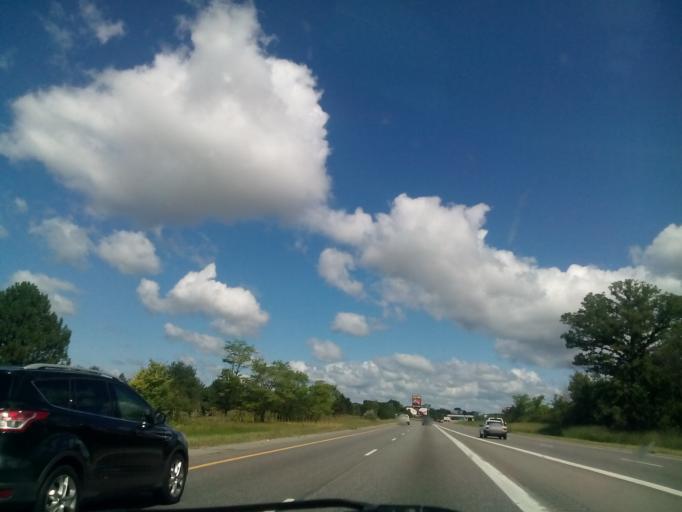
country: US
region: Michigan
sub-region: Genesee County
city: Flint
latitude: 42.9535
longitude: -83.7234
